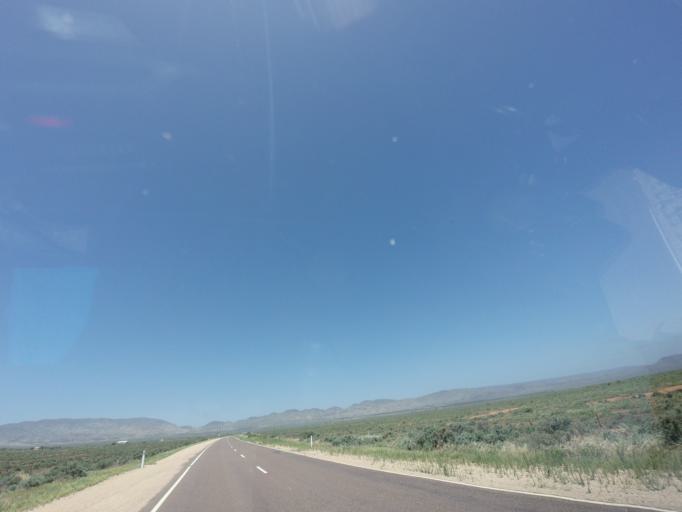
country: AU
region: South Australia
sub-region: Port Augusta
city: Port Augusta
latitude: -32.6263
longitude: 137.9244
